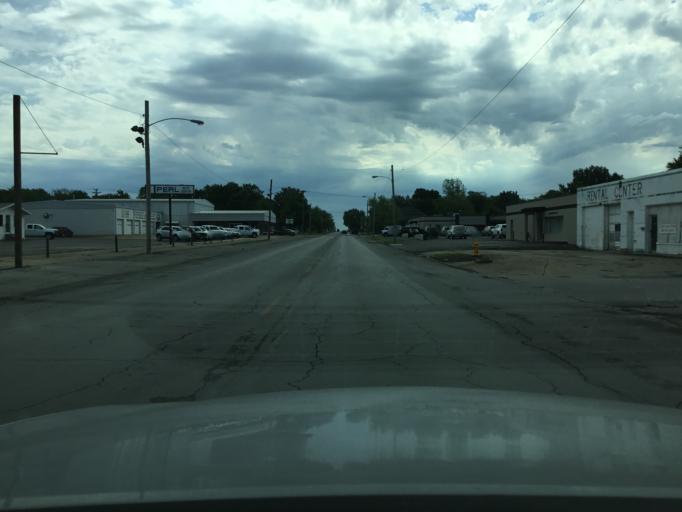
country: US
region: Kansas
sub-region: Montgomery County
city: Coffeyville
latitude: 37.0362
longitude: -95.6291
